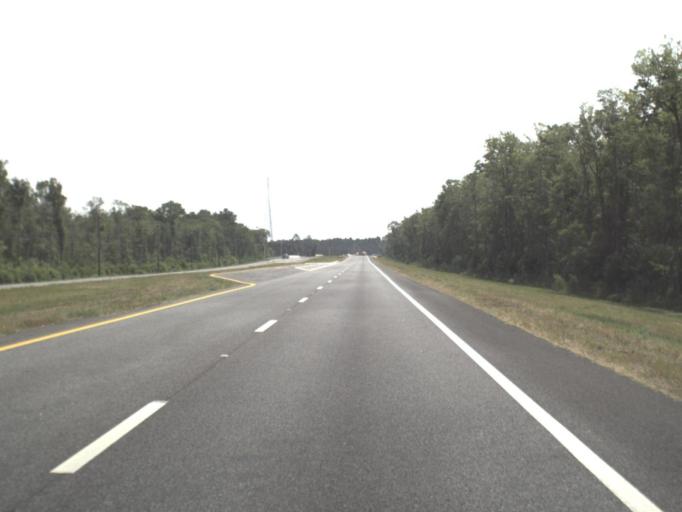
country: US
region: Florida
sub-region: Nassau County
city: Callahan
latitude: 30.6058
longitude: -81.7463
